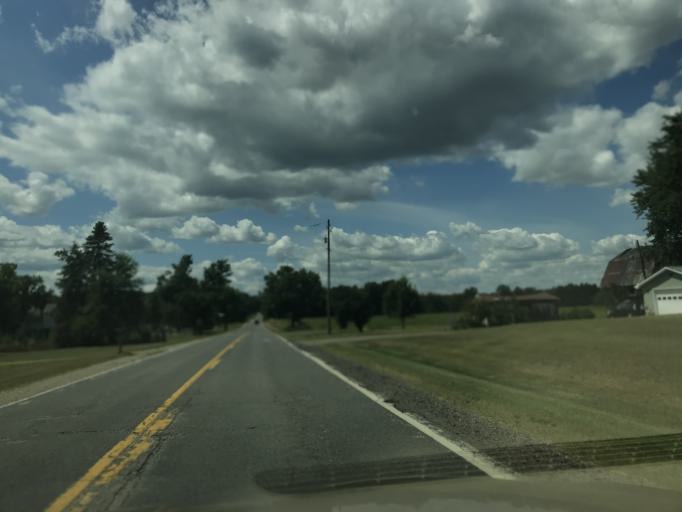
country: US
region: Michigan
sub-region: Ingham County
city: Leslie
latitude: 42.4509
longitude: -84.5361
